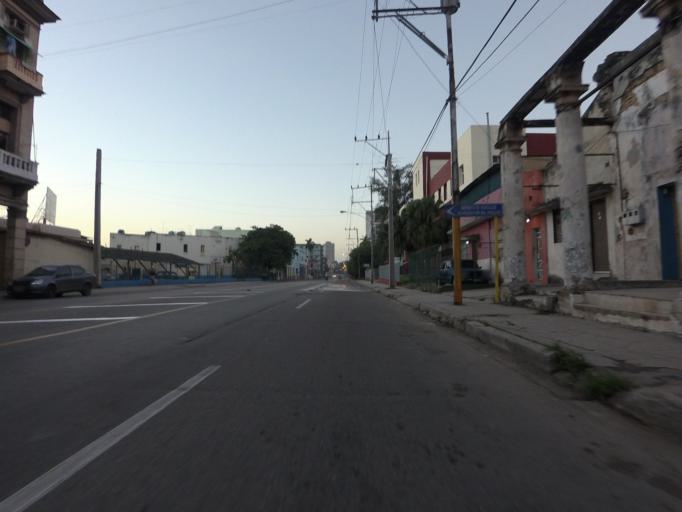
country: CU
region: La Habana
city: Havana
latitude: 23.1257
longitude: -82.3751
